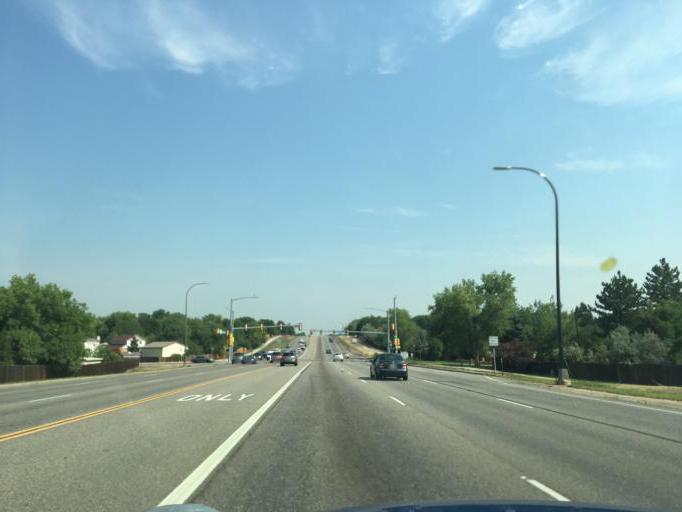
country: US
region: Colorado
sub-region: Jefferson County
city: Arvada
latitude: 39.8458
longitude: -105.0818
